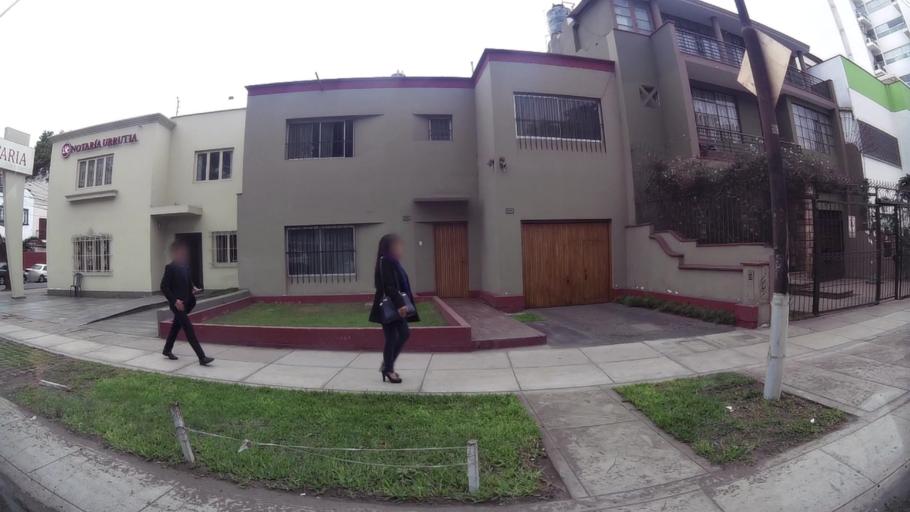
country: PE
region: Lima
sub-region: Lima
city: Surco
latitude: -12.1262
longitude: -77.0192
